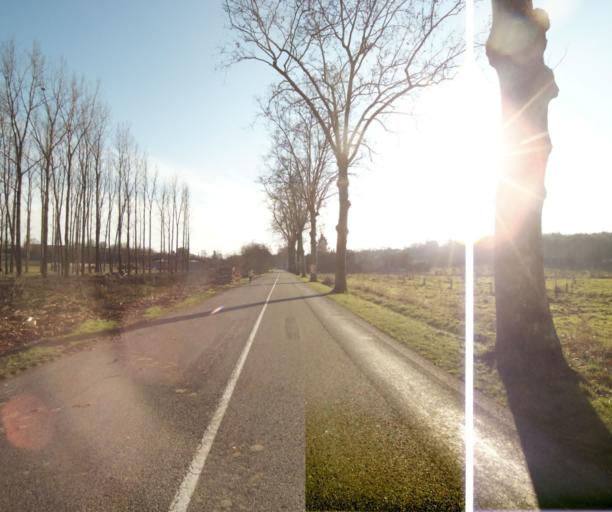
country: FR
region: Midi-Pyrenees
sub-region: Departement du Tarn-et-Garonne
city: Moissac
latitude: 44.1262
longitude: 1.1037
